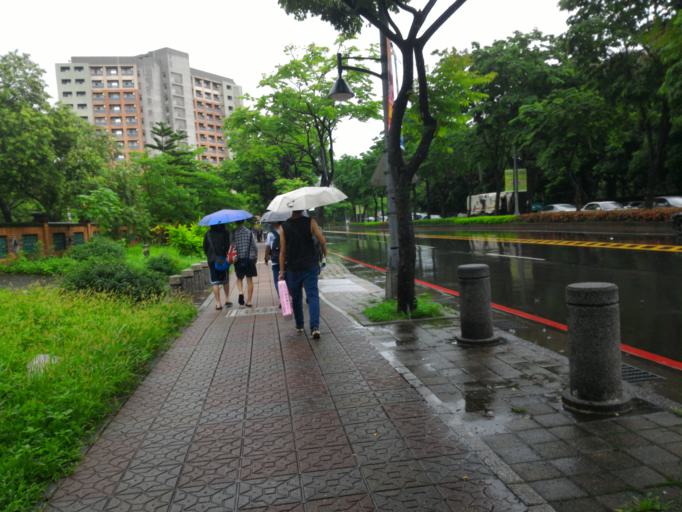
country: TW
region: Taiwan
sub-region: Taoyuan
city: Taoyuan
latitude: 24.9396
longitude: 121.3683
